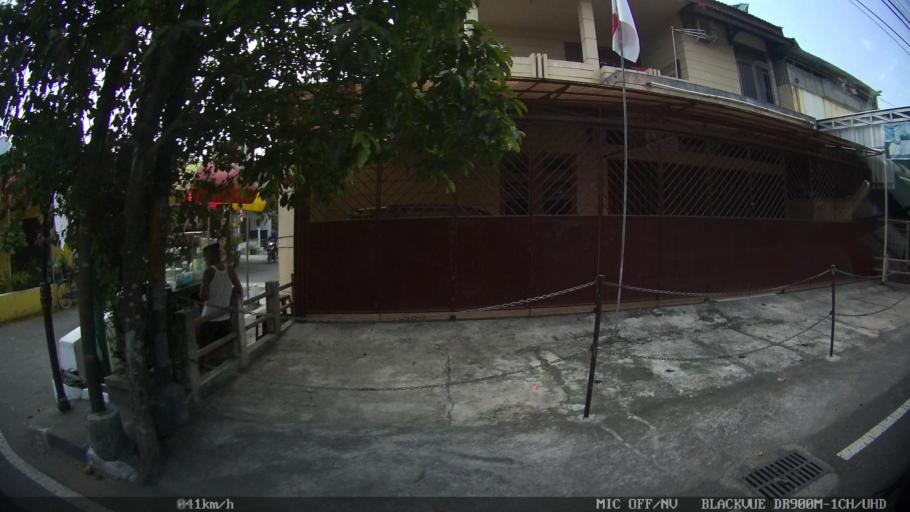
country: ID
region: Daerah Istimewa Yogyakarta
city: Yogyakarta
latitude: -7.8182
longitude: 110.3921
